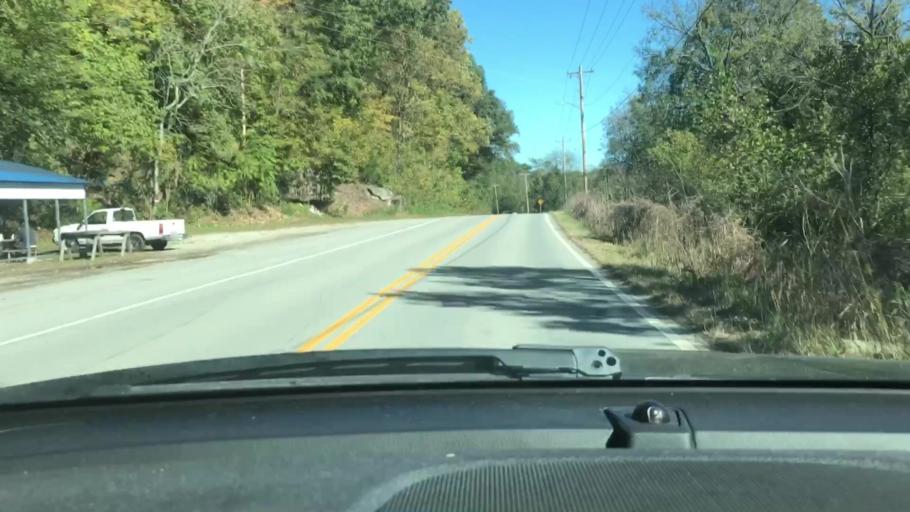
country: US
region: Tennessee
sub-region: Dickson County
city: Charlotte
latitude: 36.1815
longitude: -87.3196
